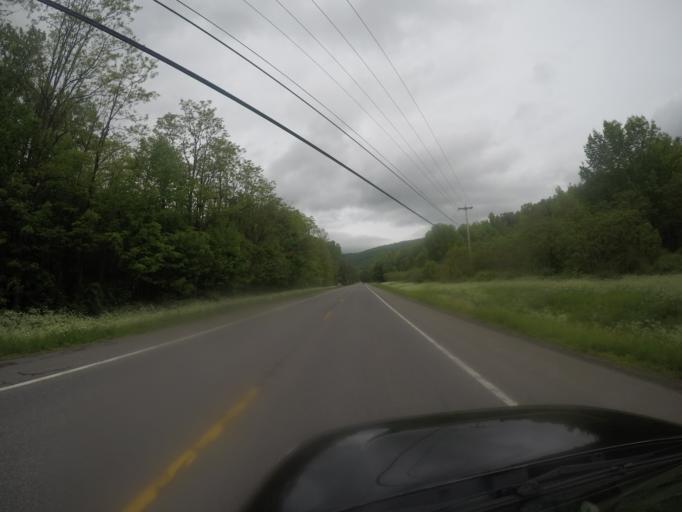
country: US
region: New York
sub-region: Ulster County
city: Shokan
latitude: 42.1070
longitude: -74.3519
